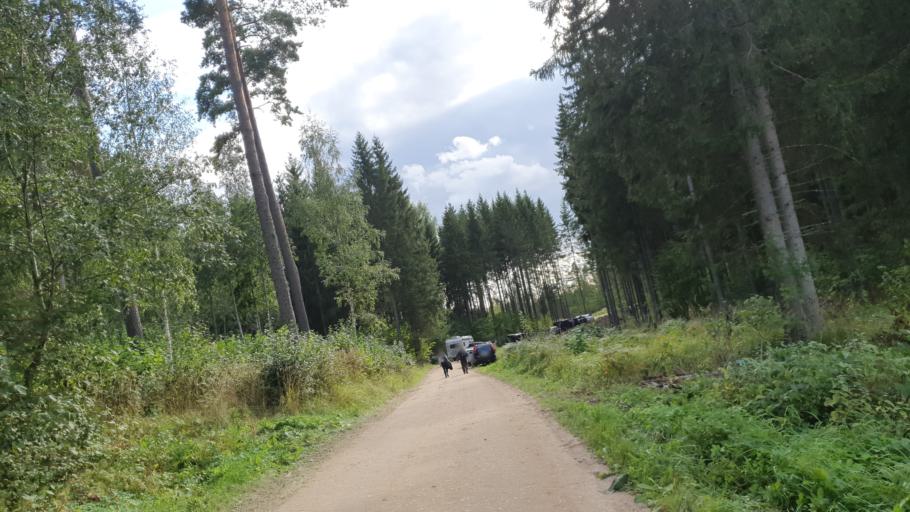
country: EE
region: Tartu
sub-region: UElenurme vald
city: Ulenurme
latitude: 58.1277
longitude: 26.7432
